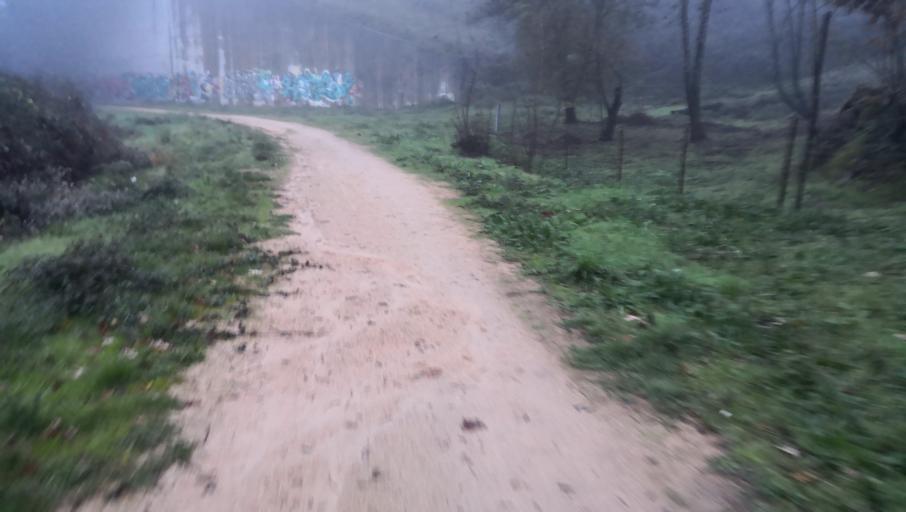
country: PT
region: Vila Real
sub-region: Vila Real
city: Vila Real
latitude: 41.3159
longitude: -7.7140
